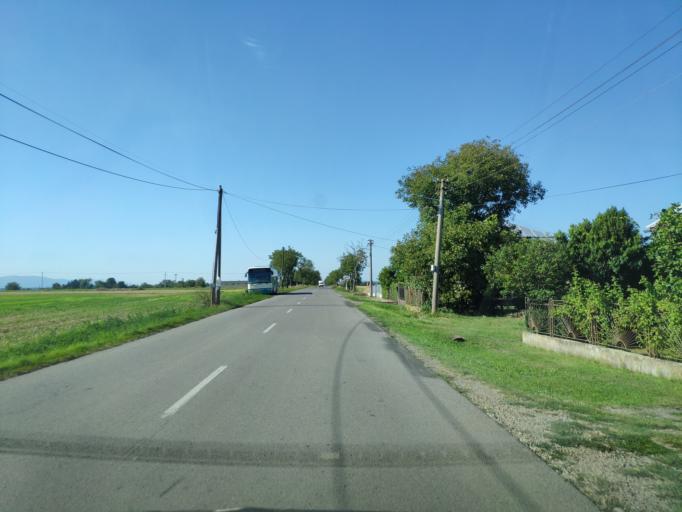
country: SK
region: Kosicky
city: Trebisov
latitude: 48.5851
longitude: 21.8490
